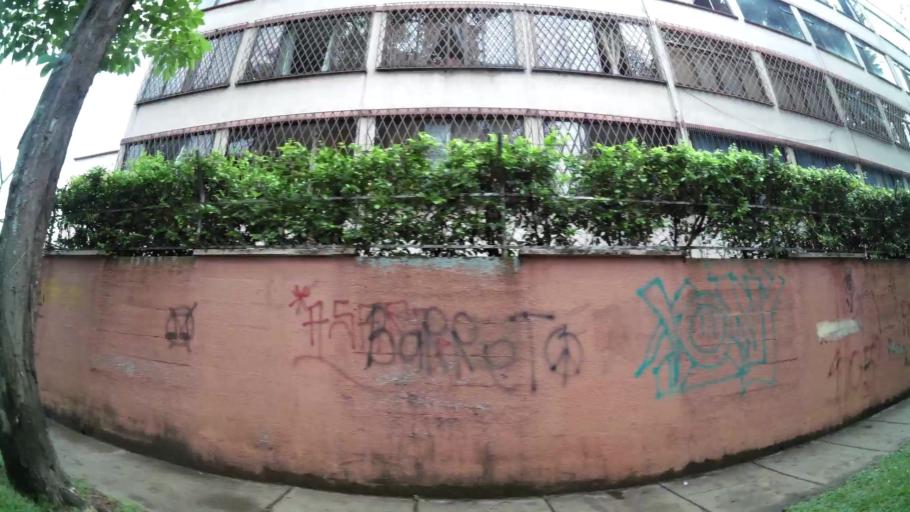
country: CO
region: Valle del Cauca
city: Cali
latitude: 3.3892
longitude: -76.5477
